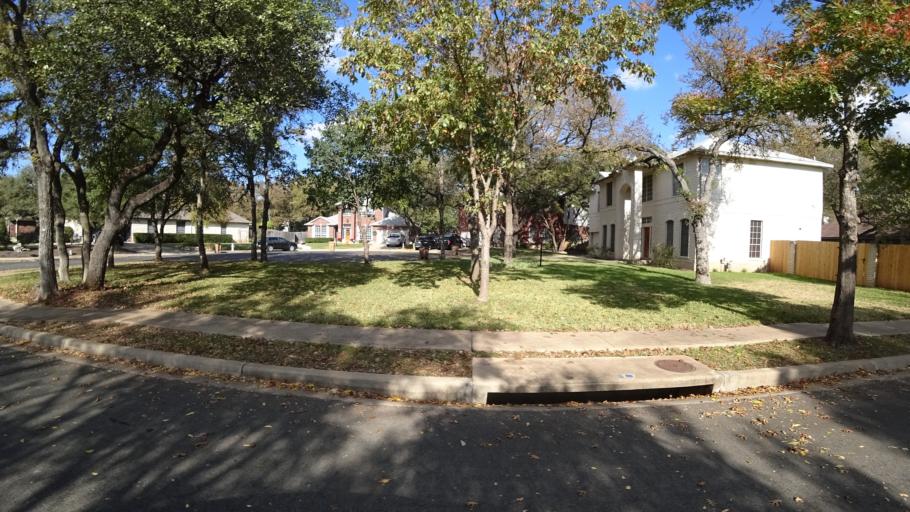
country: US
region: Texas
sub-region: Travis County
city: Shady Hollow
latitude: 30.1814
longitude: -97.8545
